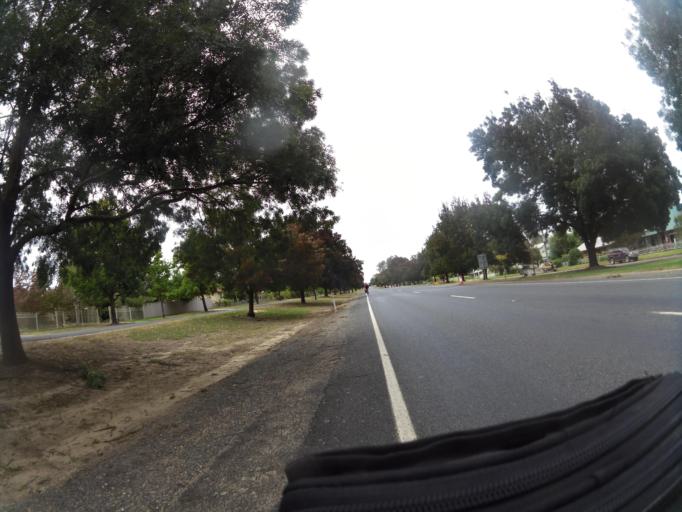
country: AU
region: New South Wales
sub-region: Snowy River
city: Jindabyne
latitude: -36.1876
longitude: 147.9164
